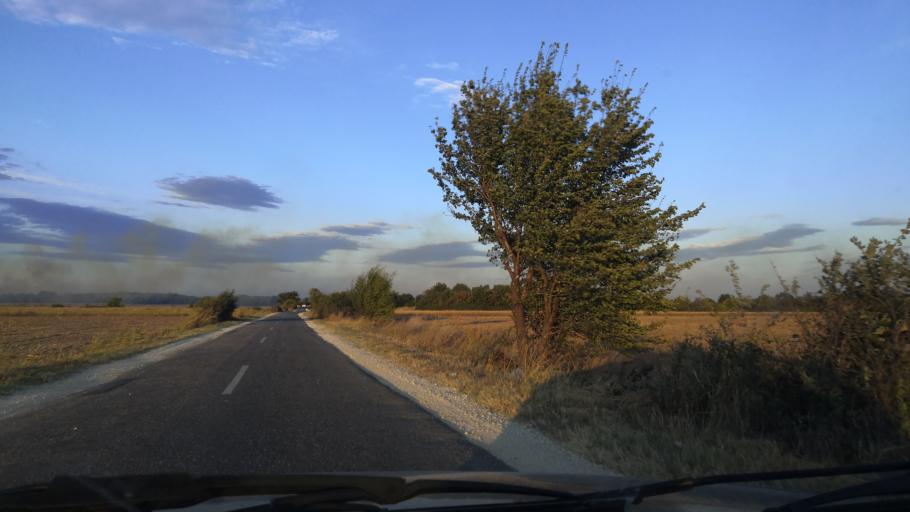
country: RS
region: Central Serbia
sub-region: Borski Okrug
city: Negotin
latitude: 44.2485
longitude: 22.5839
